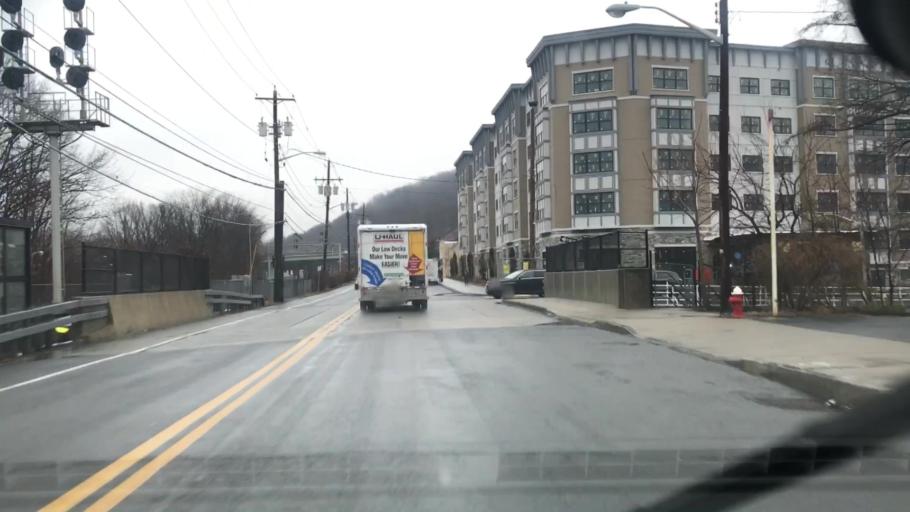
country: US
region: New York
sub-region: Rockland County
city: Suffern
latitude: 41.1140
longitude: -74.1535
